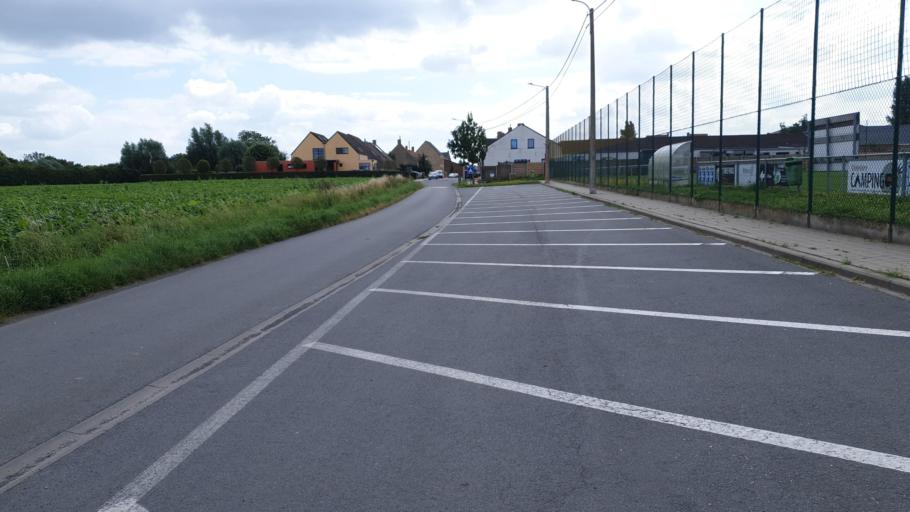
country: BE
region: Flanders
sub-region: Provincie West-Vlaanderen
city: Alveringem
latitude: 51.0156
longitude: 2.7114
